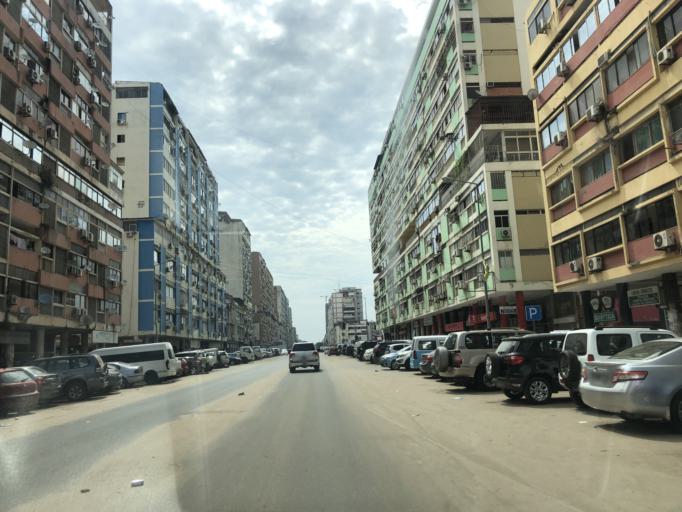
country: AO
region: Luanda
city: Luanda
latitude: -8.8194
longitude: 13.2524
